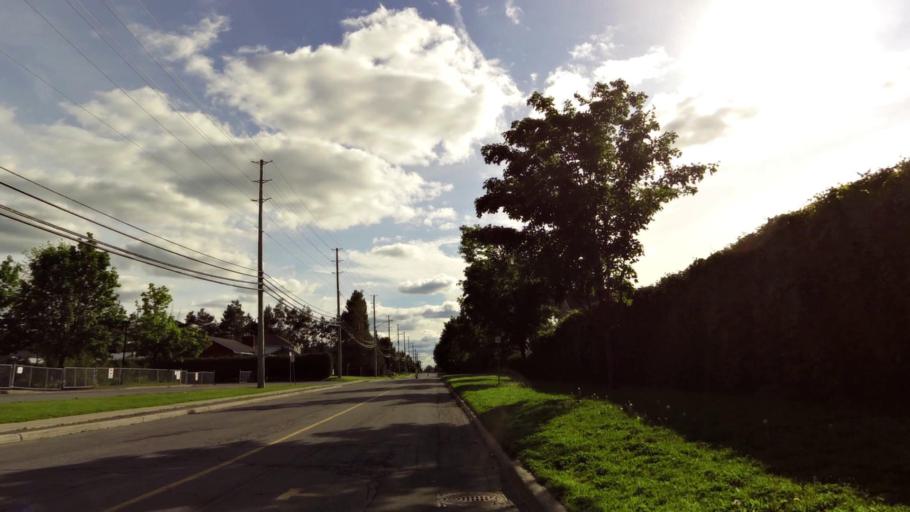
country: CA
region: Ontario
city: Ottawa
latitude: 45.2613
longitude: -75.5639
